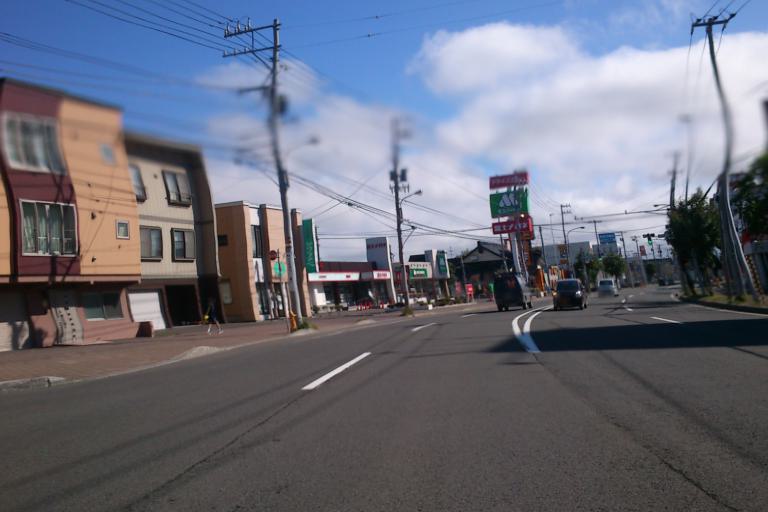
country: JP
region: Hokkaido
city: Sapporo
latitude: 43.1220
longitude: 141.2488
